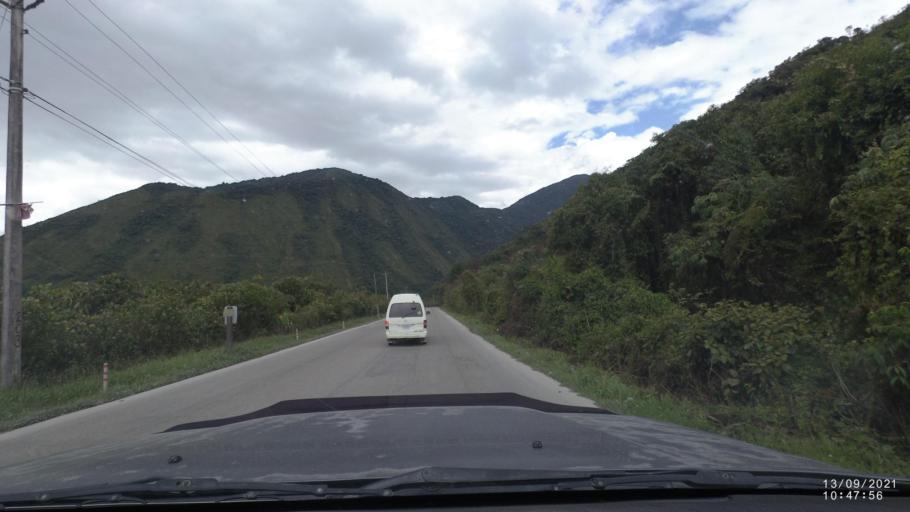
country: BO
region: Cochabamba
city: Colomi
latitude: -17.1981
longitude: -65.8630
